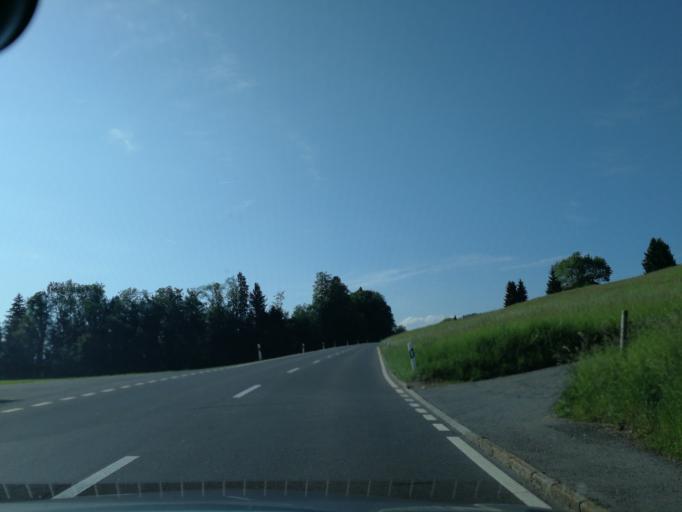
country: CH
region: Zurich
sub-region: Bezirk Horgen
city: Horgen / Allmend
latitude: 47.2355
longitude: 8.6134
